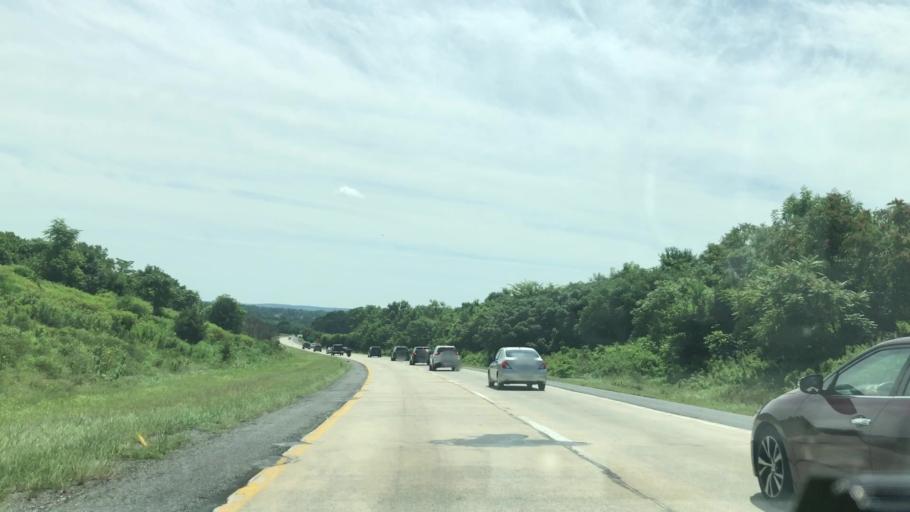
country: US
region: Pennsylvania
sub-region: Montgomery County
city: Audubon
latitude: 40.1463
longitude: -75.4591
